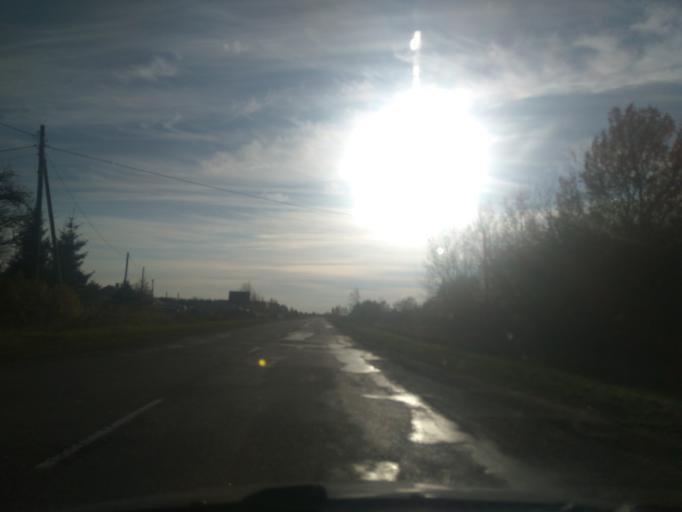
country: LV
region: Ventspils
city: Ventspils
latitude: 57.3410
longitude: 21.5683
